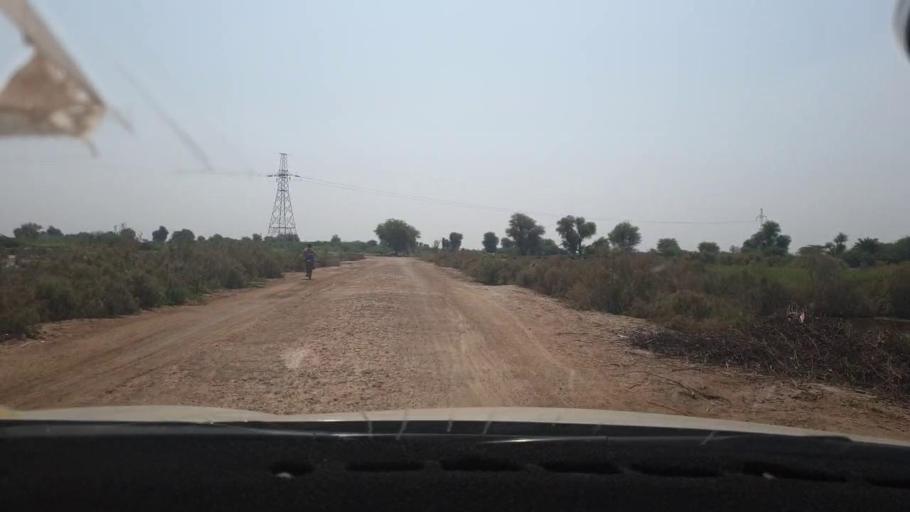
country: PK
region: Sindh
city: Tando Mittha Khan
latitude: 25.9180
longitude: 69.2348
